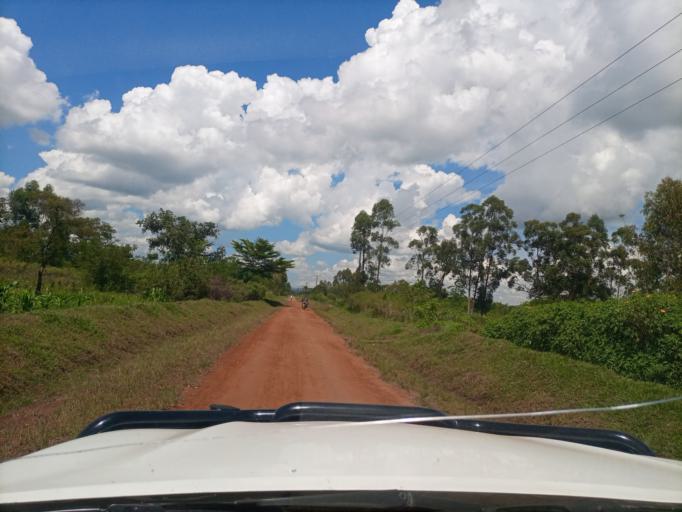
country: UG
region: Eastern Region
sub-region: Tororo District
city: Tororo
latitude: 0.6554
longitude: 33.9989
